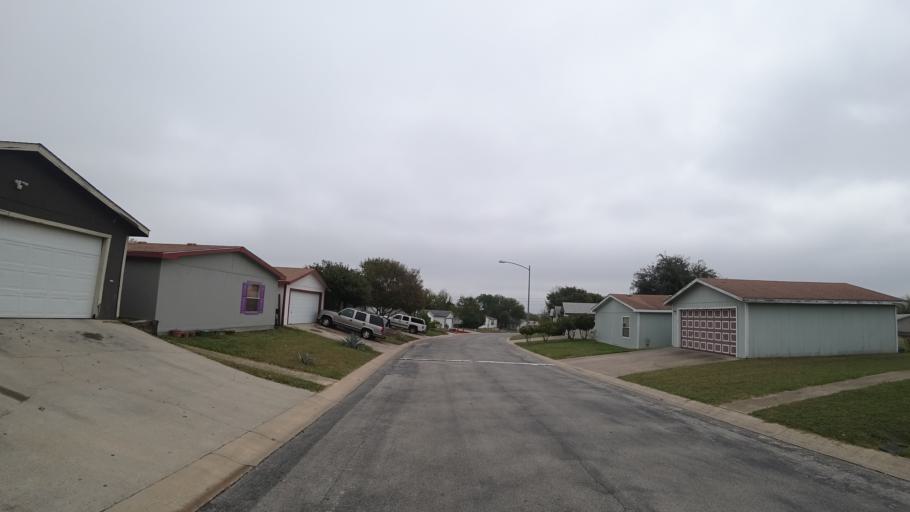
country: US
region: Texas
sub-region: Travis County
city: Pflugerville
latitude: 30.3918
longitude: -97.6411
